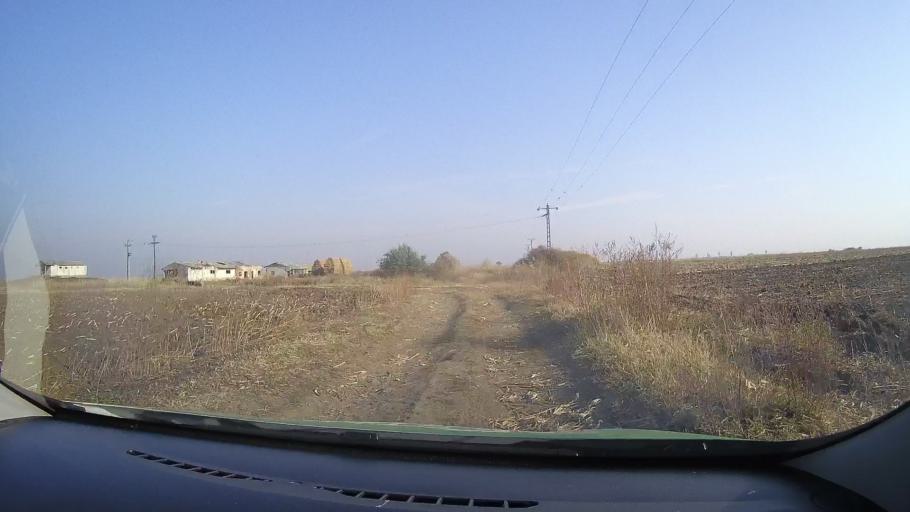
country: RO
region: Arad
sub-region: Comuna Pilu
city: Pilu
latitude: 46.5442
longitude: 21.3296
